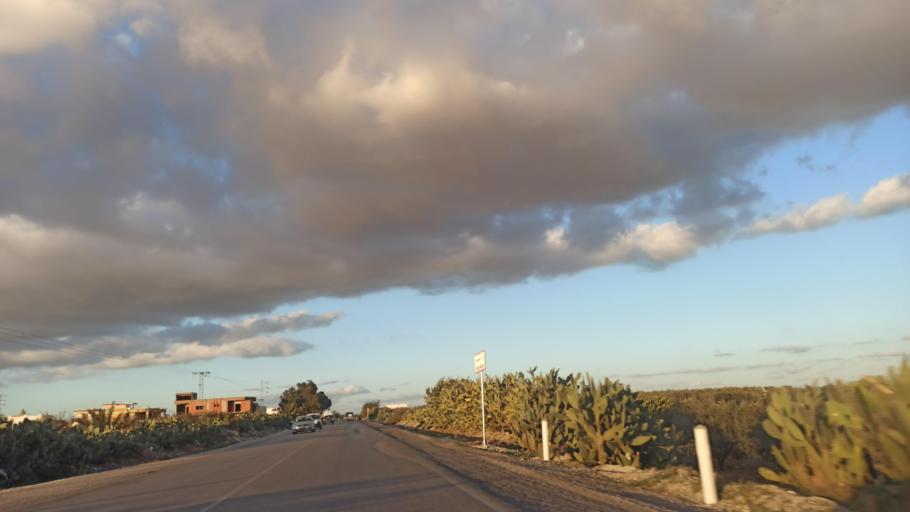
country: TN
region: Susah
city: Sidi Bou Ali
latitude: 36.0061
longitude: 10.3169
